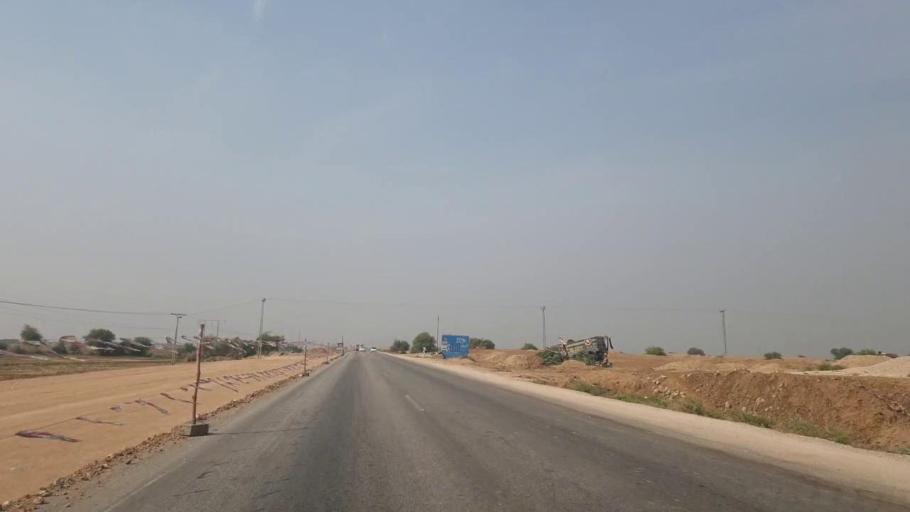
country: PK
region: Sindh
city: Sann
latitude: 26.1218
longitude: 68.0584
